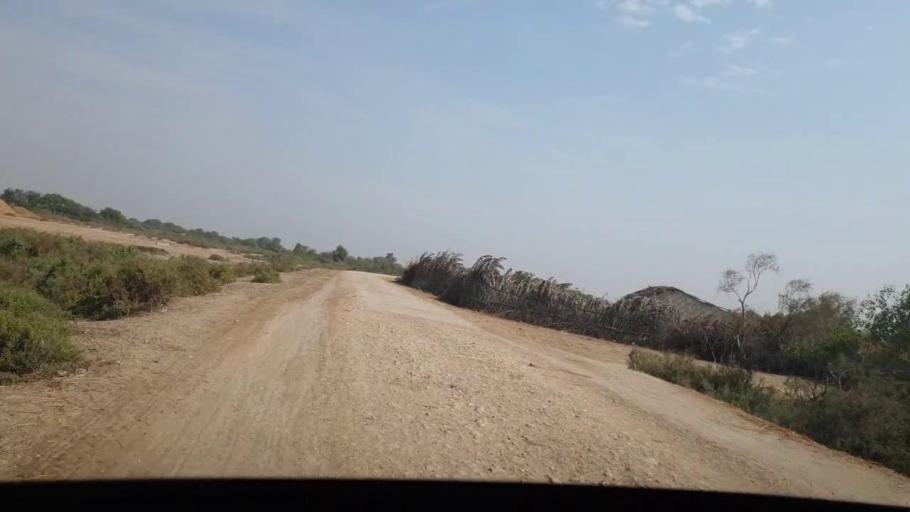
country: PK
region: Sindh
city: Chuhar Jamali
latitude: 24.2696
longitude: 67.9308
